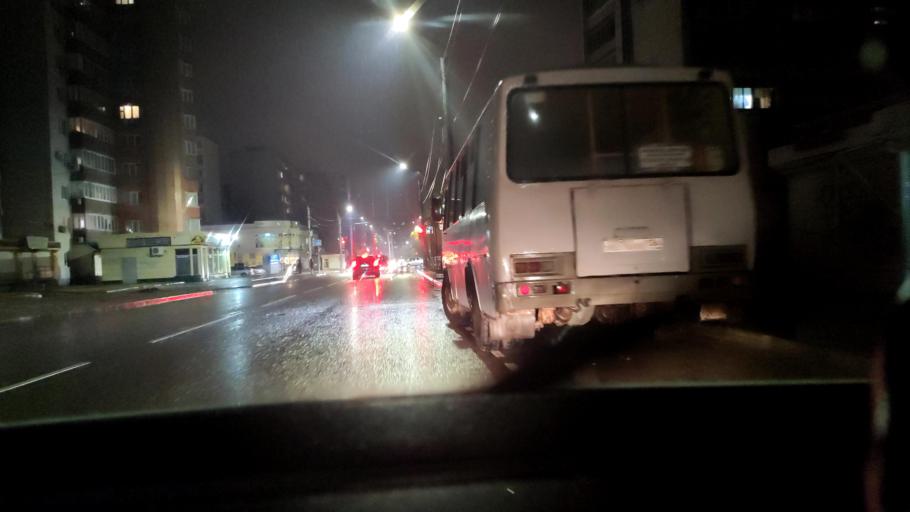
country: RU
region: Voronezj
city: Pridonskoy
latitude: 51.6507
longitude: 39.1209
